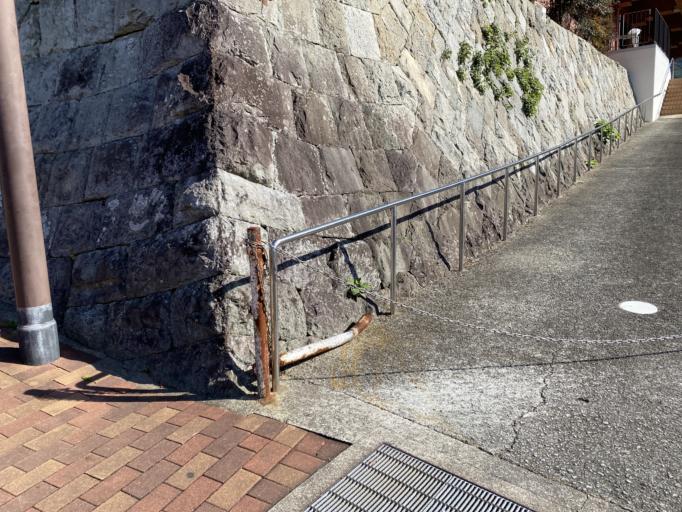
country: JP
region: Nagasaki
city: Nagasaki-shi
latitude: 32.7759
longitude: 129.8674
